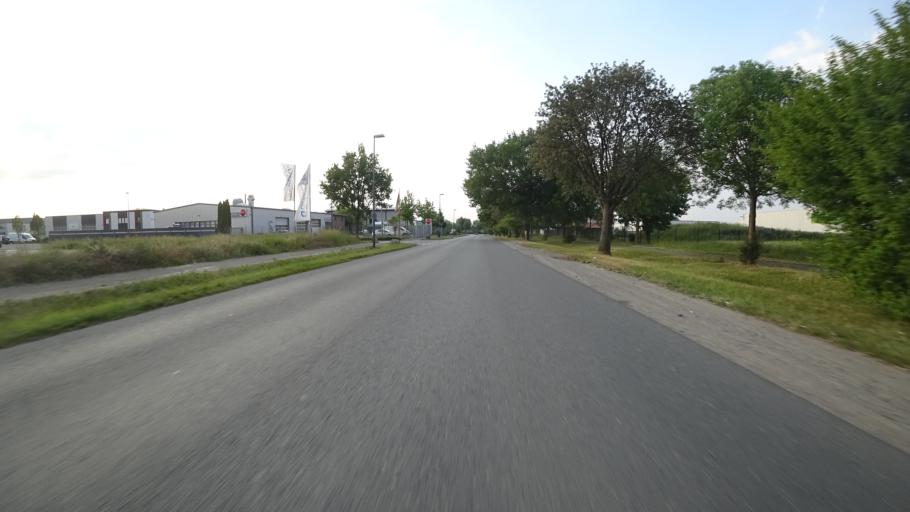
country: DE
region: North Rhine-Westphalia
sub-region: Regierungsbezirk Arnsberg
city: Lippstadt
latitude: 51.6513
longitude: 8.3573
